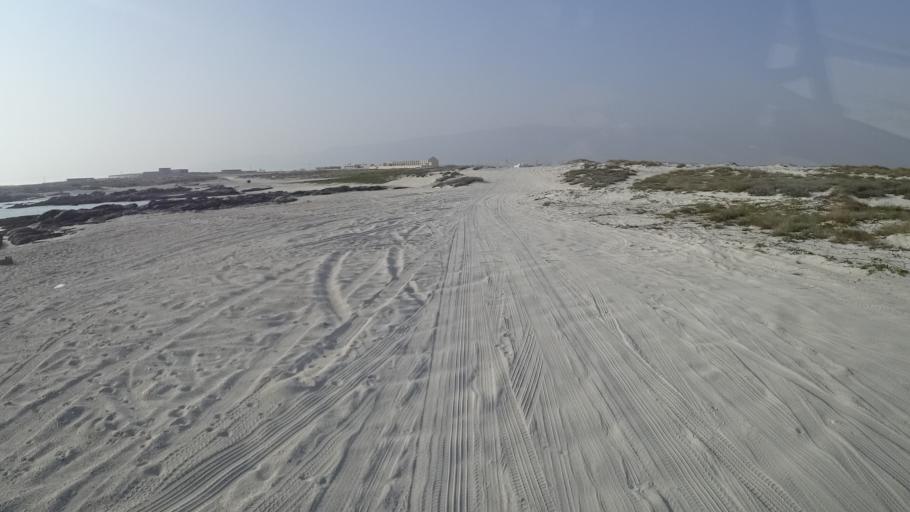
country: OM
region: Zufar
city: Salalah
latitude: 16.9678
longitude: 54.7060
